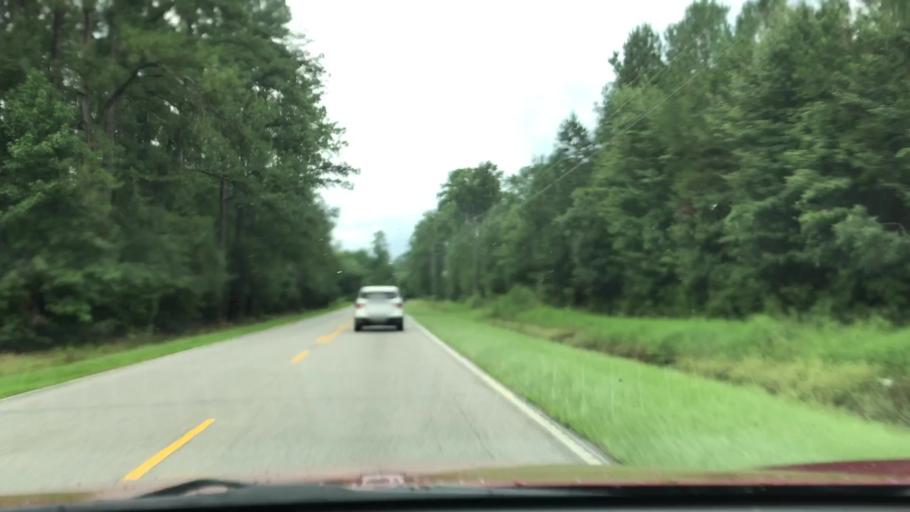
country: US
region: South Carolina
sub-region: Georgetown County
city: Murrells Inlet
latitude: 33.6229
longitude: -79.1920
